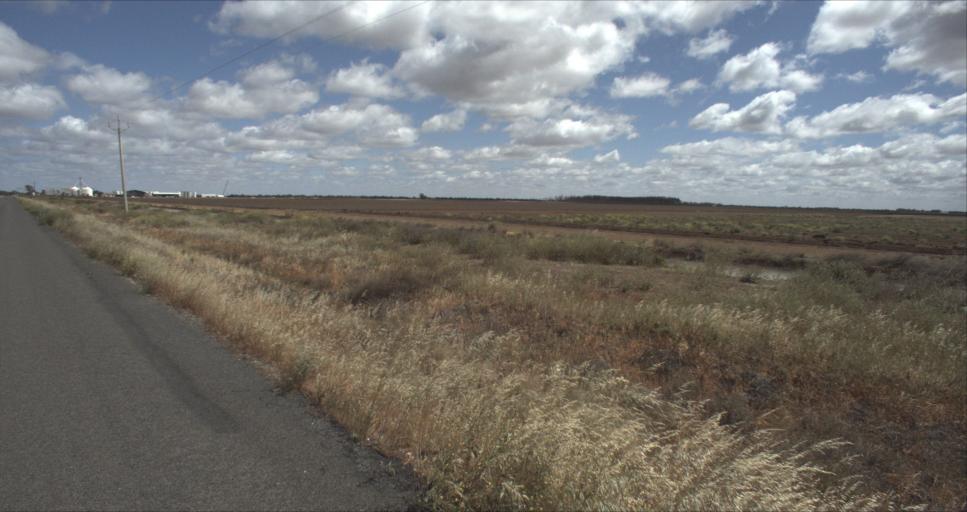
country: AU
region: New South Wales
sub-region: Murrumbidgee Shire
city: Darlington Point
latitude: -34.5775
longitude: 146.1892
